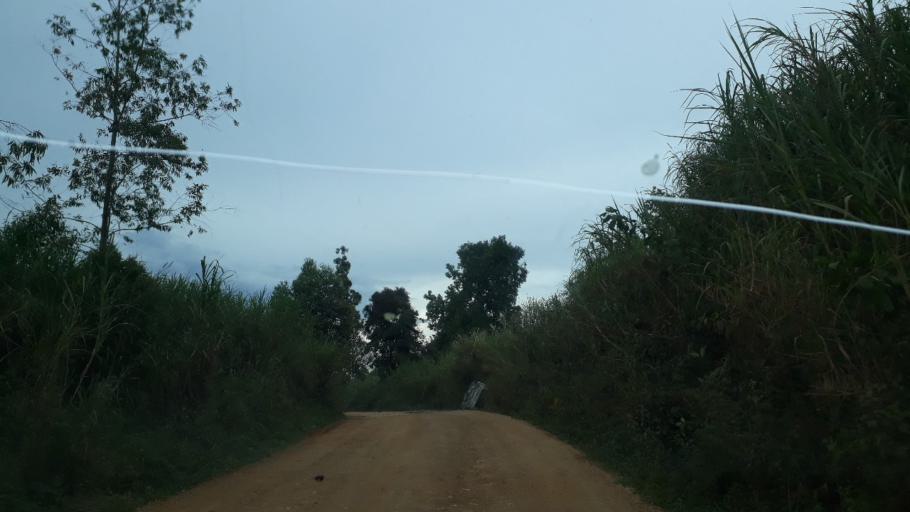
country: CD
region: Eastern Province
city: Bunia
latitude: 1.9296
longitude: 30.5155
